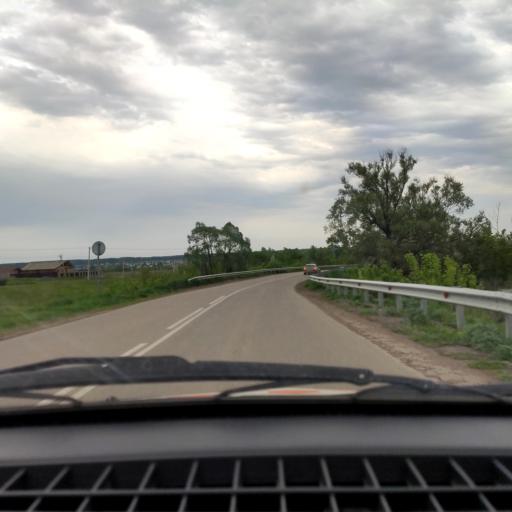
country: RU
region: Bashkortostan
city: Avdon
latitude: 54.5594
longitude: 55.7634
